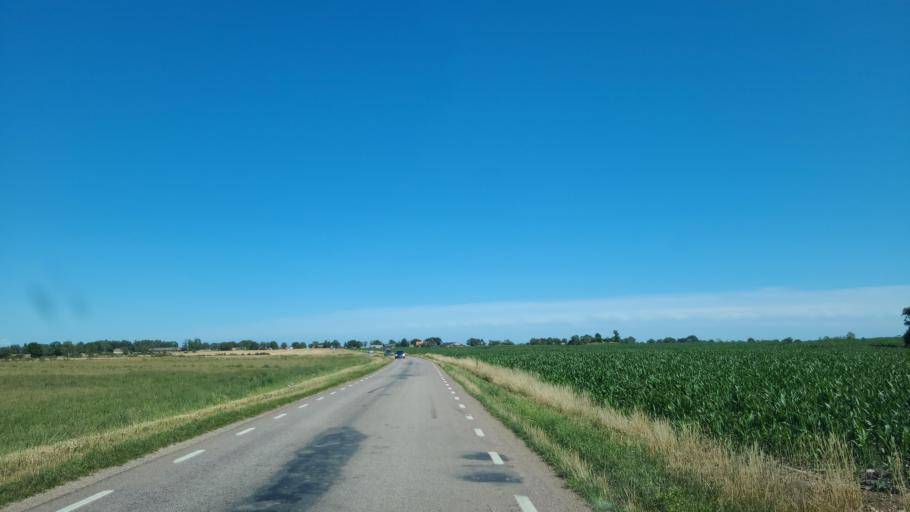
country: SE
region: Kalmar
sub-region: Borgholms Kommun
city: Borgholm
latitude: 56.7807
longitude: 16.7186
